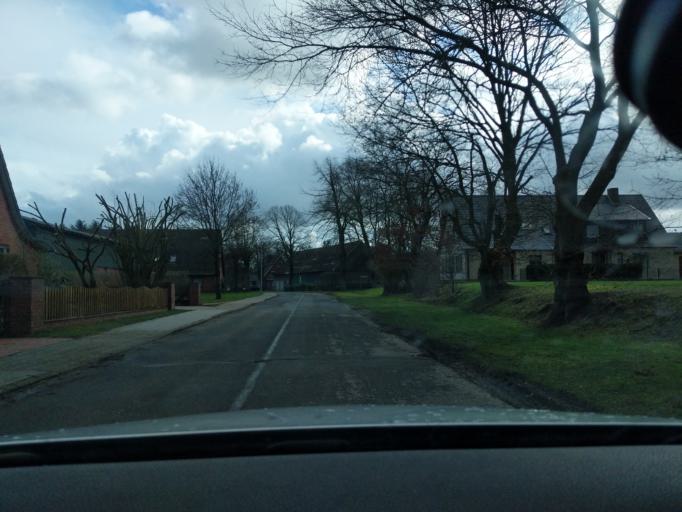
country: DE
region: Lower Saxony
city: Kranenburg
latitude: 53.6075
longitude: 9.2029
